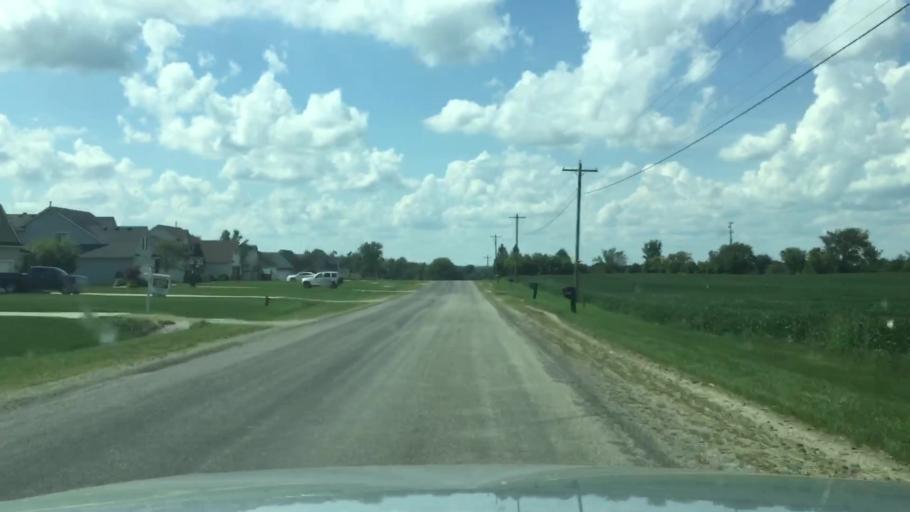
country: US
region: Michigan
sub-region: Lenawee County
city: Clinton
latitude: 42.0725
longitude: -83.9507
